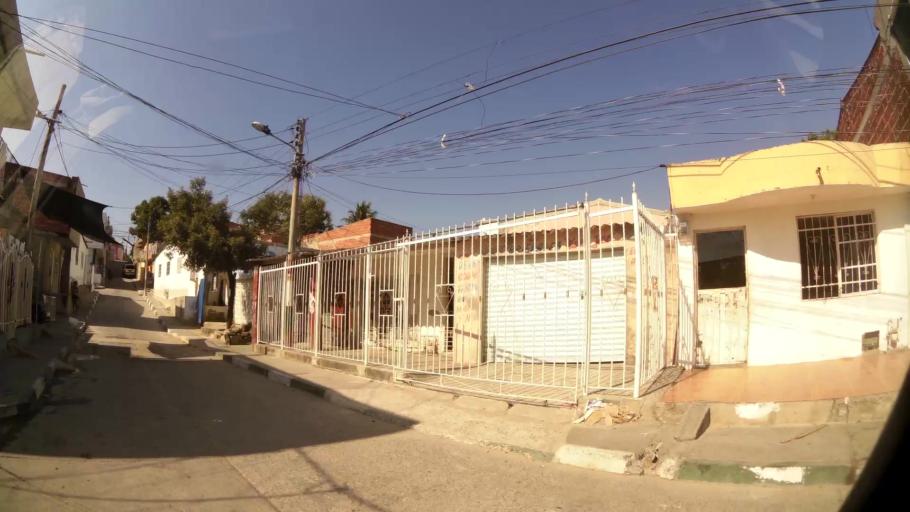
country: CO
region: Bolivar
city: Cartagena
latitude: 10.3955
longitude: -75.5009
